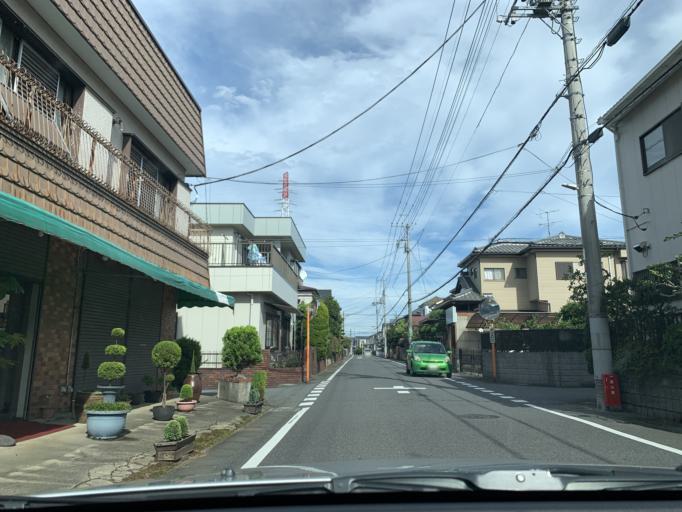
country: JP
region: Chiba
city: Nagareyama
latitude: 35.9029
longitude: 139.9228
